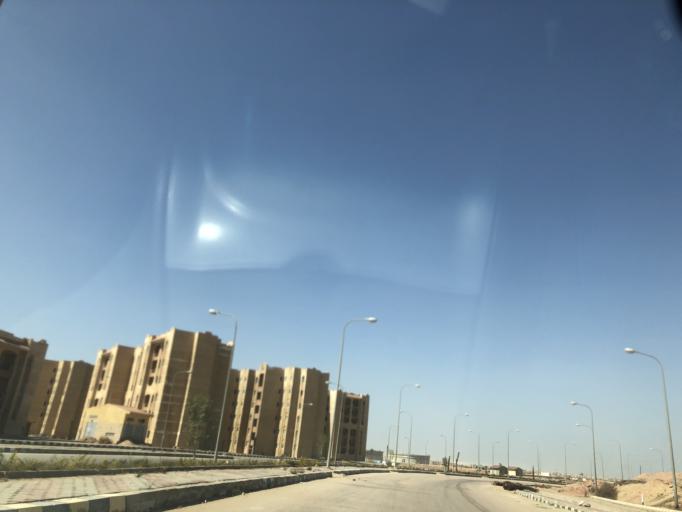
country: EG
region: Al Jizah
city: Madinat Sittah Uktubar
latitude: 29.9239
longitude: 31.0379
